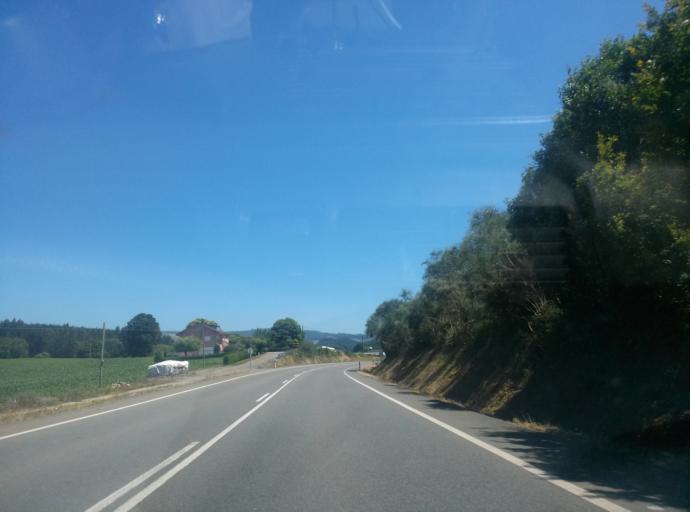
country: ES
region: Galicia
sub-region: Provincia de Lugo
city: Meira
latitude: 43.2283
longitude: -7.3319
